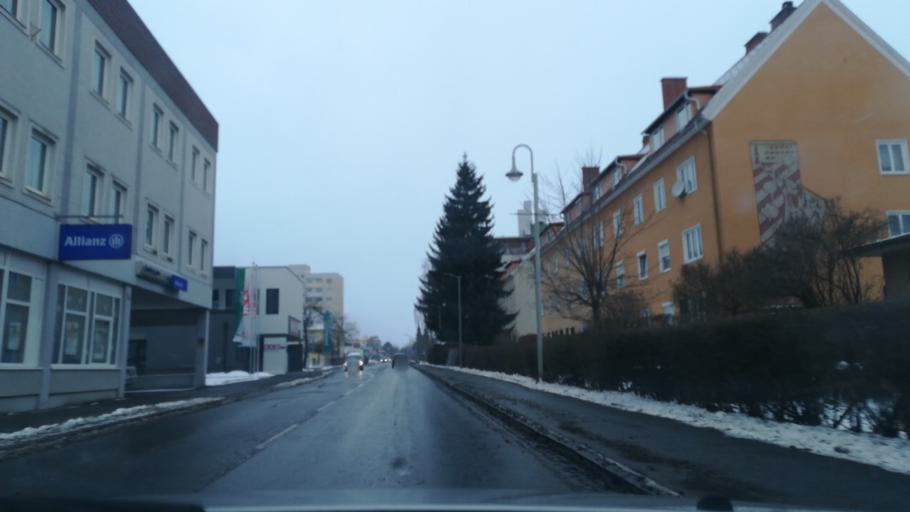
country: AT
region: Styria
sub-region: Politischer Bezirk Murtal
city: Judenburg
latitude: 47.1690
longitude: 14.6525
